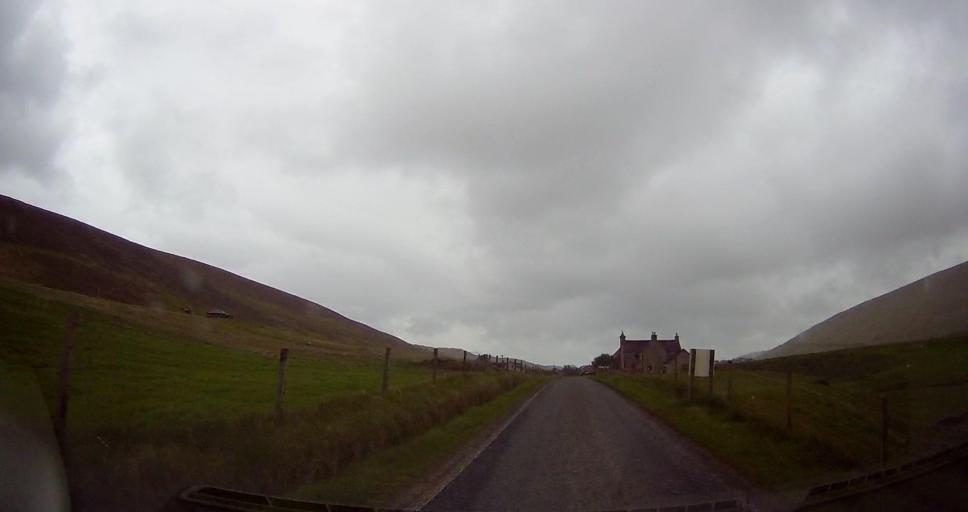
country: GB
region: Scotland
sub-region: Shetland Islands
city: Lerwick
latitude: 60.2573
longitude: -1.2887
